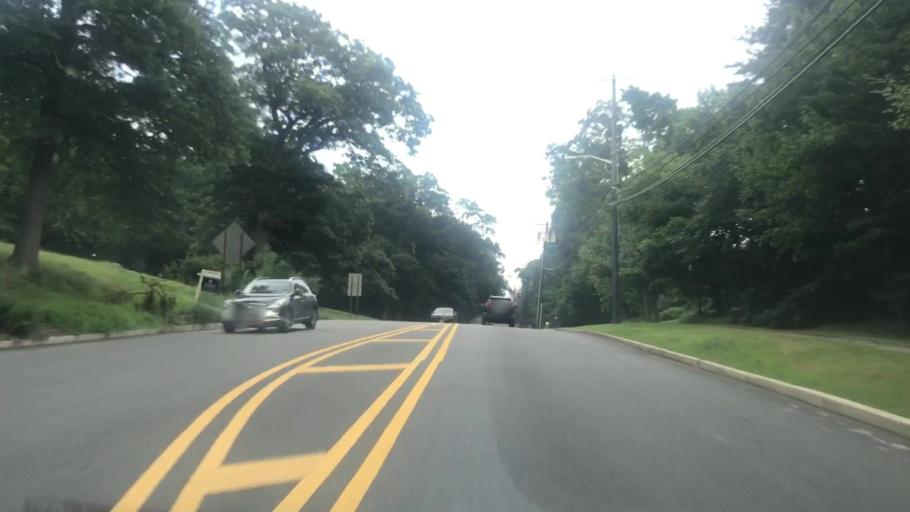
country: US
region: New Jersey
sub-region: Bergen County
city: Englewood Cliffs
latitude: 40.8858
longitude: -73.9606
